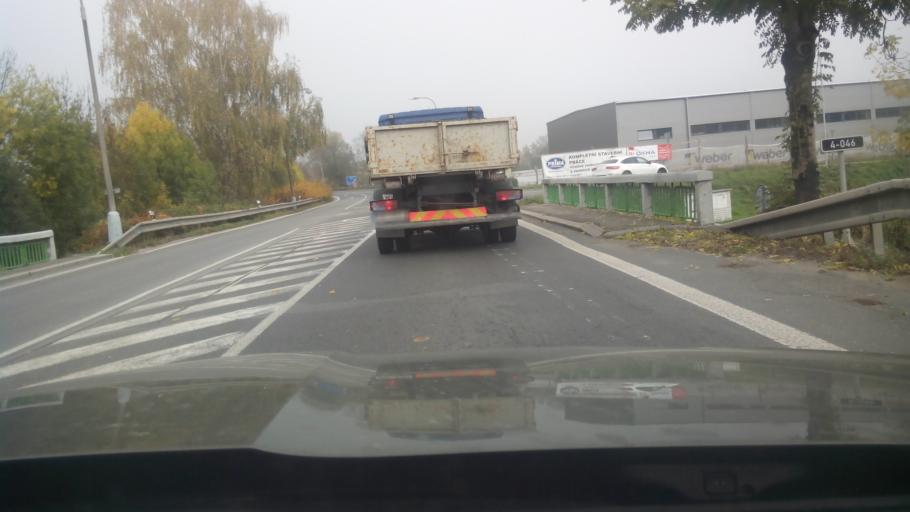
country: CZ
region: Jihocesky
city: Strakonice
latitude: 49.2625
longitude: 13.9153
